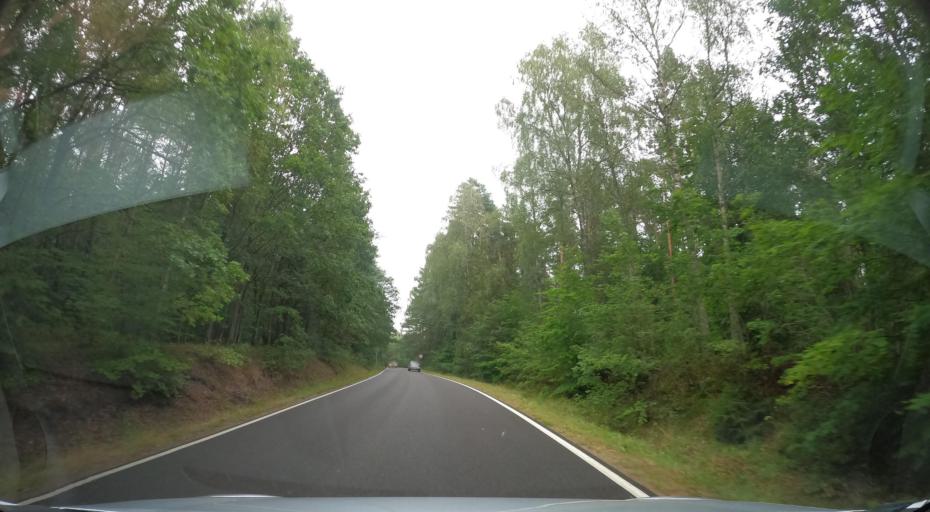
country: PL
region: Pomeranian Voivodeship
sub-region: Powiat leborski
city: Lebork
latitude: 54.4993
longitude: 17.8363
